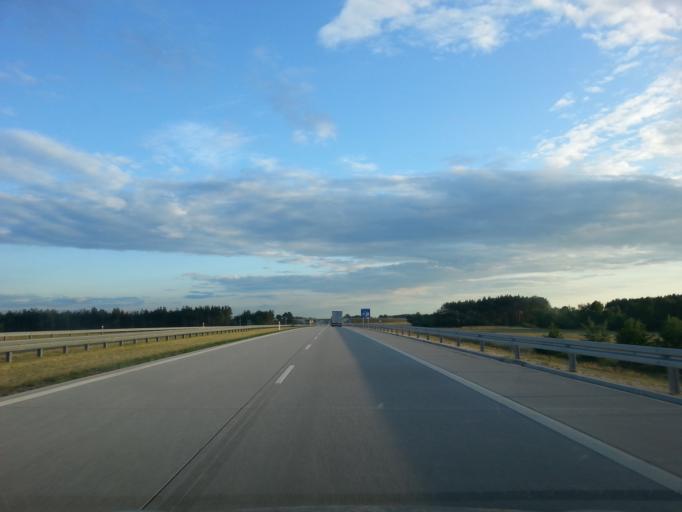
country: PL
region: Lodz Voivodeship
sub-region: Powiat sieradzki
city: Zloczew
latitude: 51.3760
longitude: 18.5454
